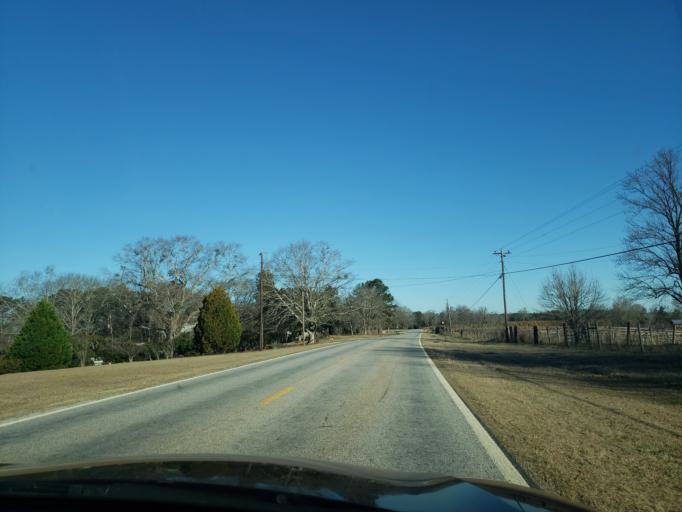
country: US
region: Alabama
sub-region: Elmore County
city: Tallassee
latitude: 32.5931
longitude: -85.7995
